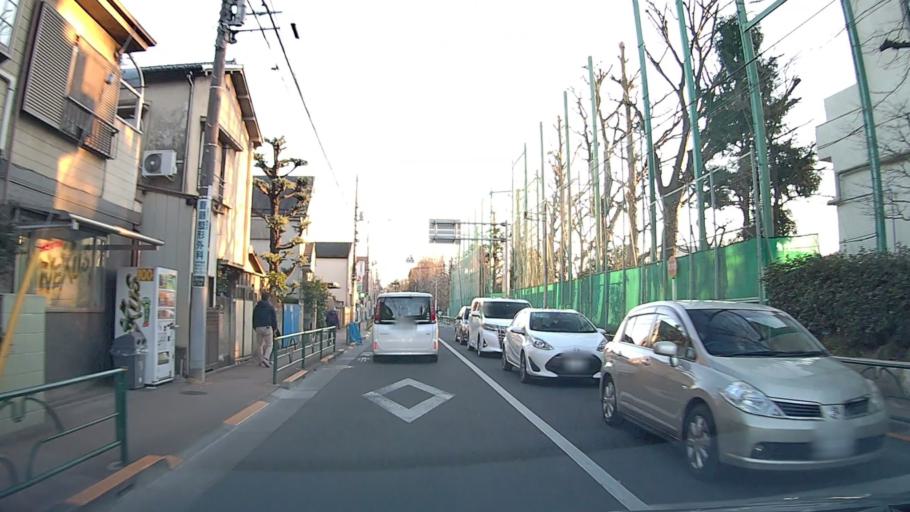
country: JP
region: Tokyo
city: Musashino
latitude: 35.7417
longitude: 139.5968
